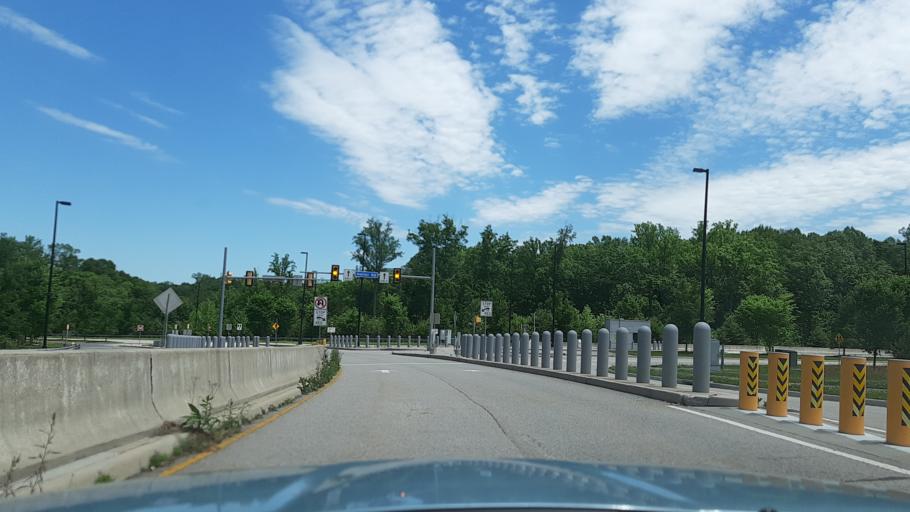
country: US
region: Virginia
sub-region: Fairfax County
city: Newington
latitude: 38.7496
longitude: -77.2046
